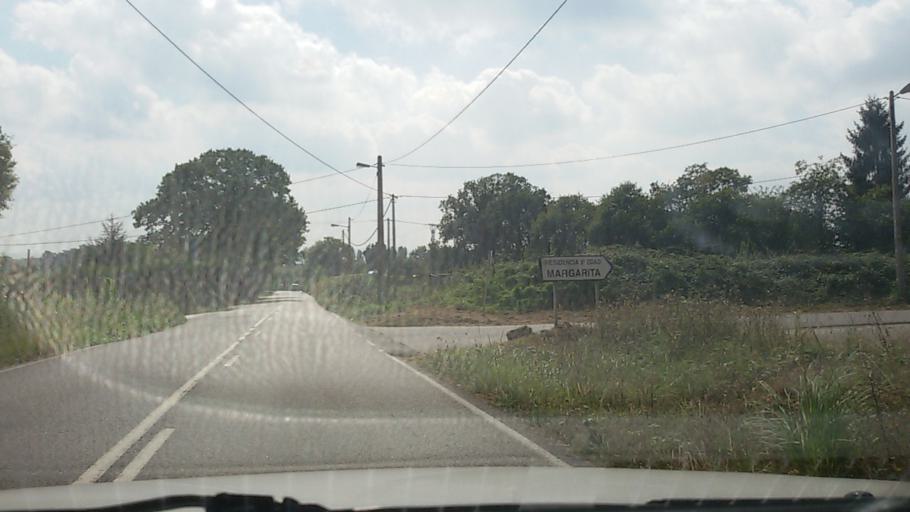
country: ES
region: Asturias
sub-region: Province of Asturias
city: Lugones
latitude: 43.4381
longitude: -5.8059
